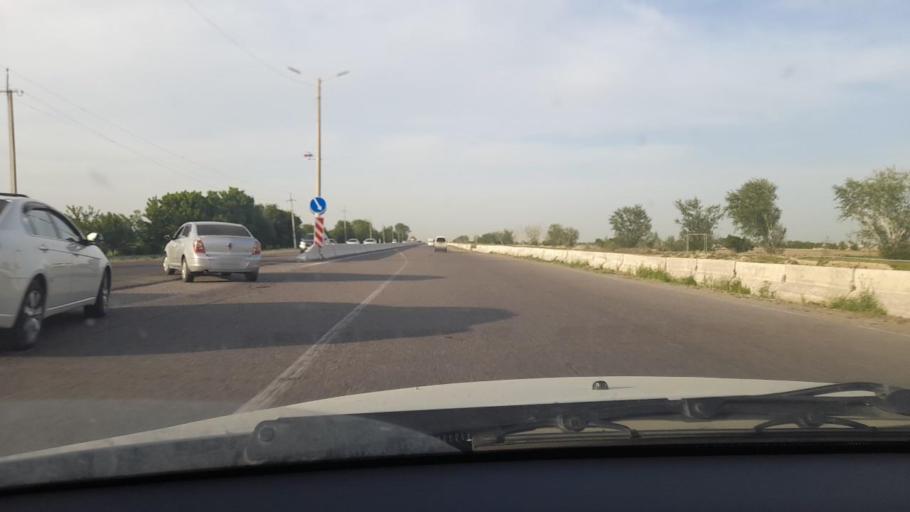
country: UZ
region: Jizzax
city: Gagarin
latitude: 40.4980
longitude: 68.3058
